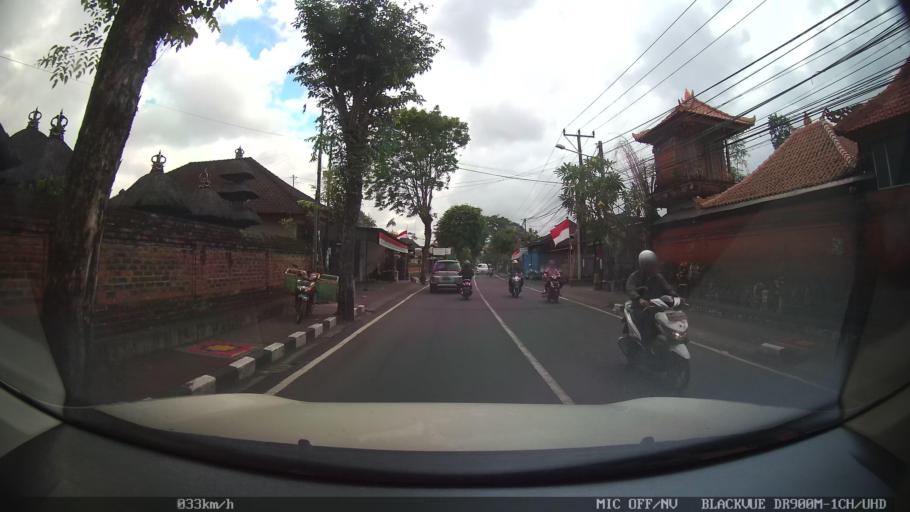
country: ID
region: Bali
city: Banjar Gunungpande
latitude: -8.6508
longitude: 115.1686
